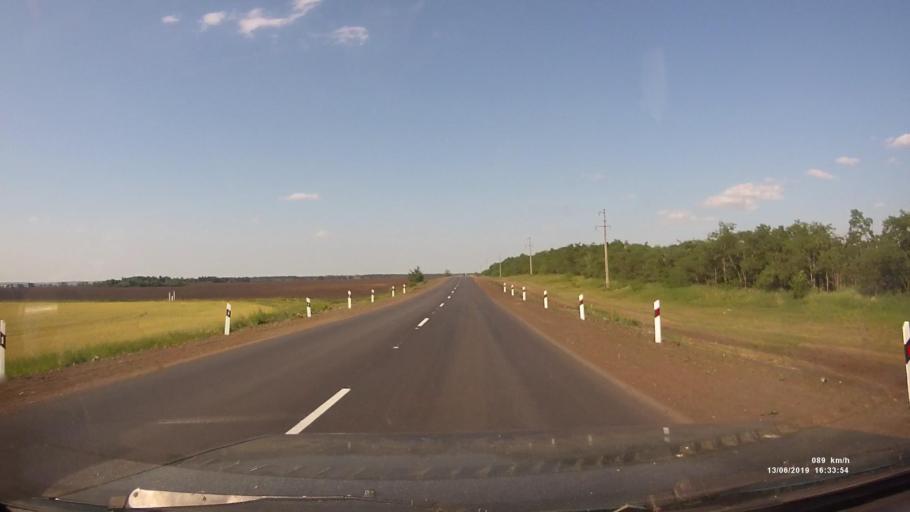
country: RU
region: Rostov
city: Kazanskaya
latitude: 49.8659
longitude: 41.2855
